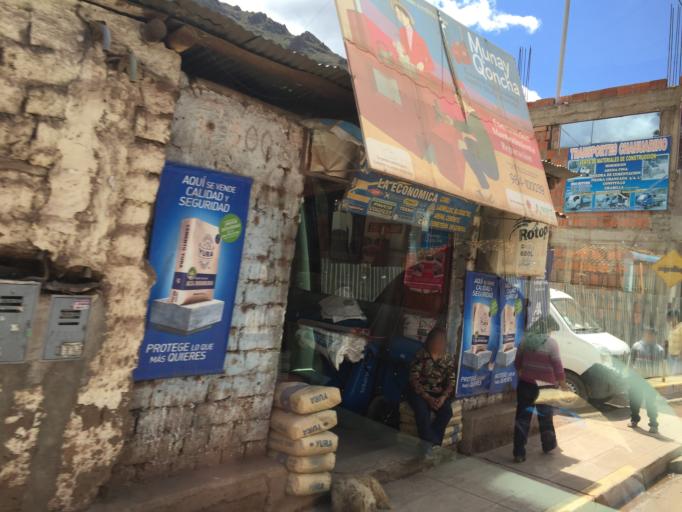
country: PE
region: Cusco
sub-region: Provincia de Calca
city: Pisac
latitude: -13.4229
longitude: -71.8520
